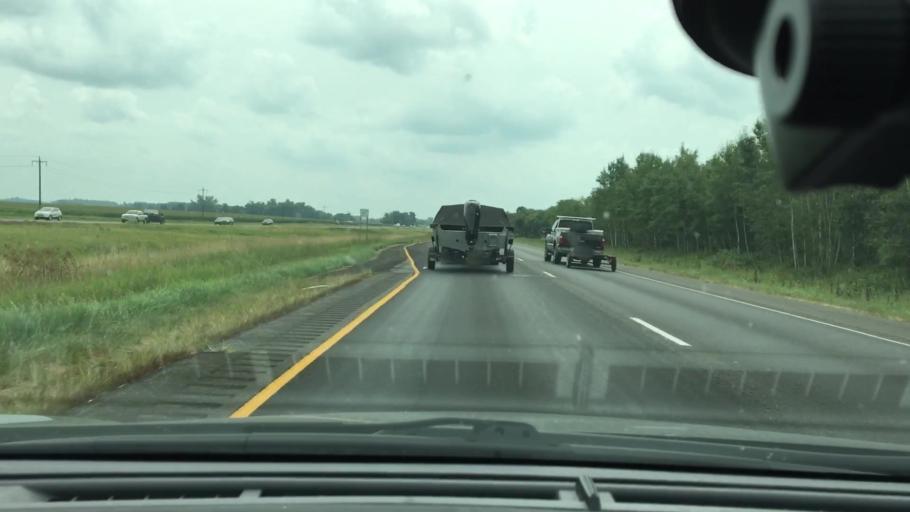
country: US
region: Minnesota
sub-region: Mille Lacs County
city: Princeton
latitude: 45.6336
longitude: -93.6177
